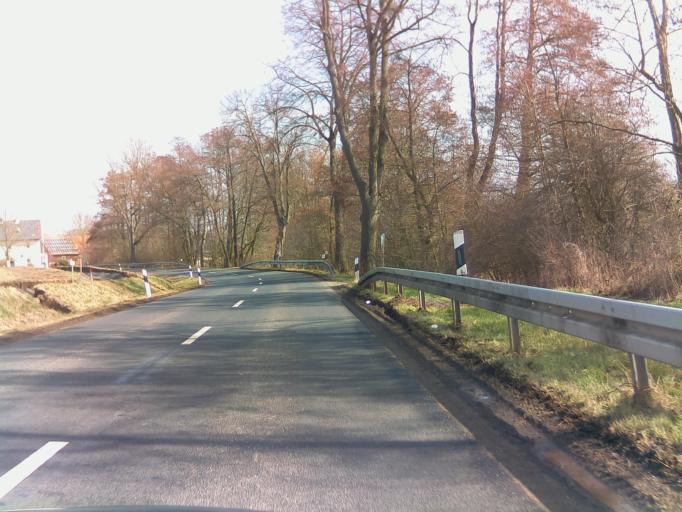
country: DE
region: Hesse
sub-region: Regierungsbezirk Giessen
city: Alsfeld
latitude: 50.6897
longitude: 9.3003
